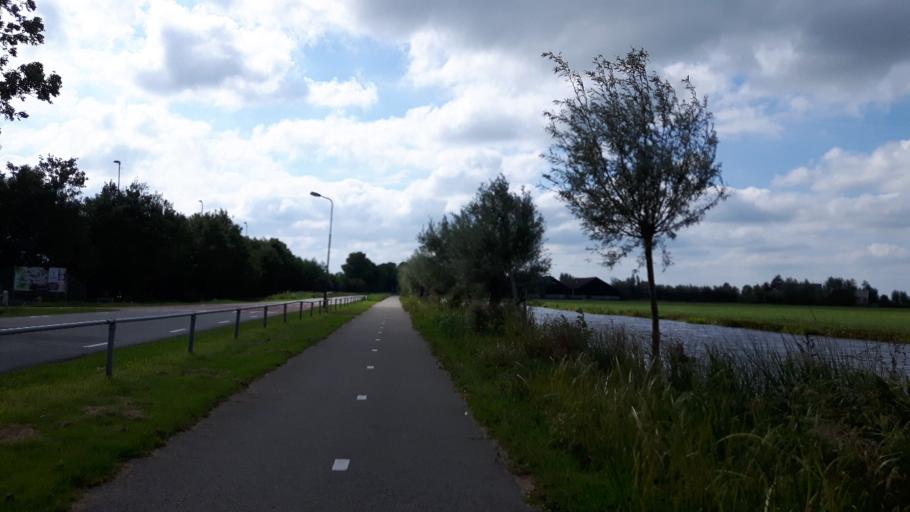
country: NL
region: Utrecht
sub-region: Gemeente Woerden
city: Woerden
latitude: 52.1214
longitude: 4.8459
